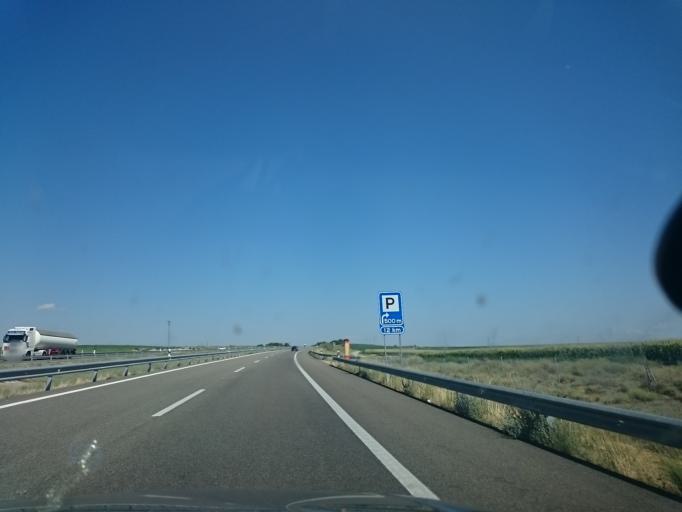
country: ES
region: Aragon
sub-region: Provincia de Huesca
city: Valfarta
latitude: 41.5195
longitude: -0.1090
